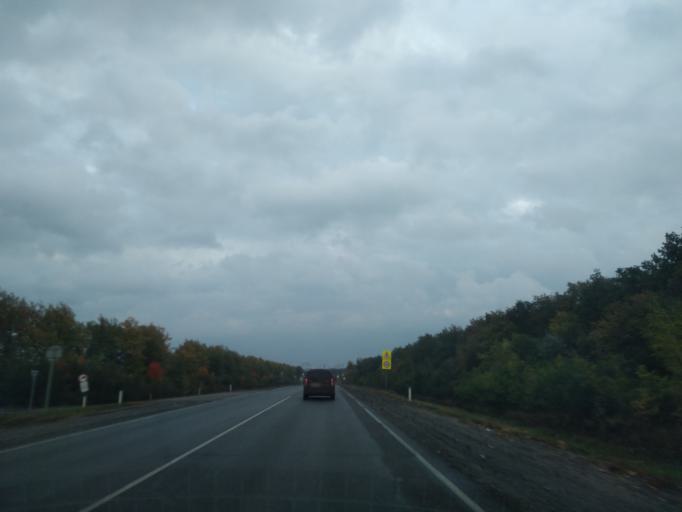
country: RU
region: Lipetsk
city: Syrskoye
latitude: 52.6015
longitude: 39.3858
